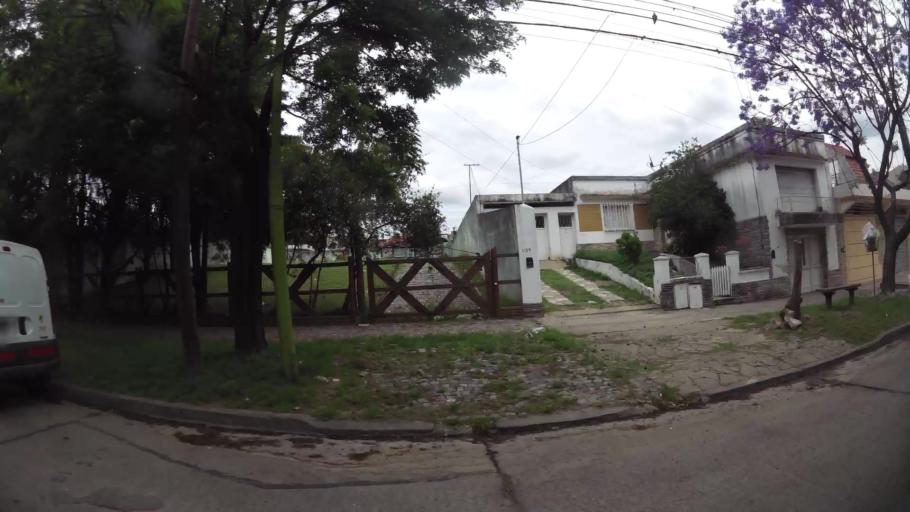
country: AR
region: Buenos Aires
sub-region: Partido de Campana
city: Campana
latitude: -34.1695
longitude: -58.9671
